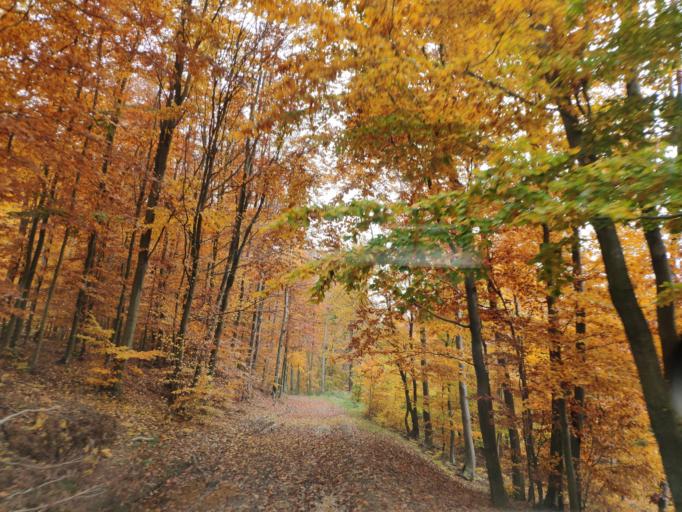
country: SK
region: Kosicky
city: Moldava nad Bodvou
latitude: 48.7324
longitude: 21.0263
